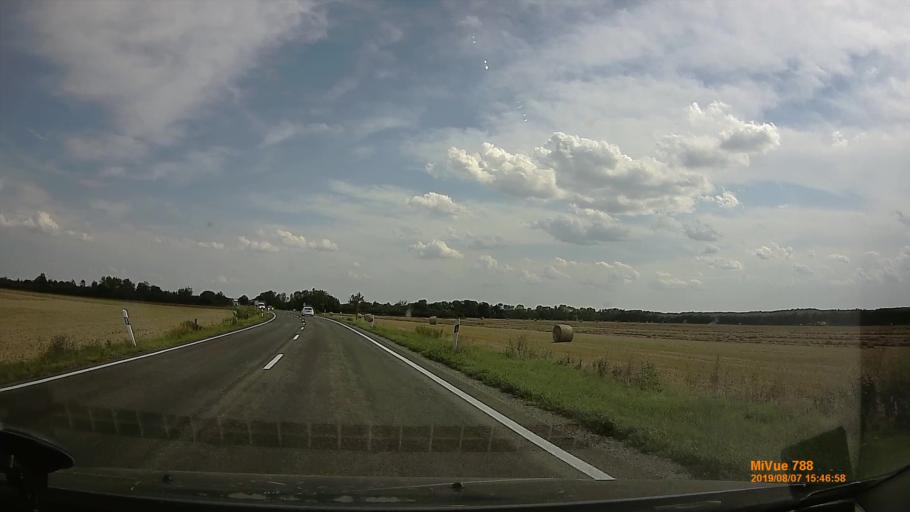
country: HU
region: Vas
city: Szombathely
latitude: 47.1779
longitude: 16.6229
